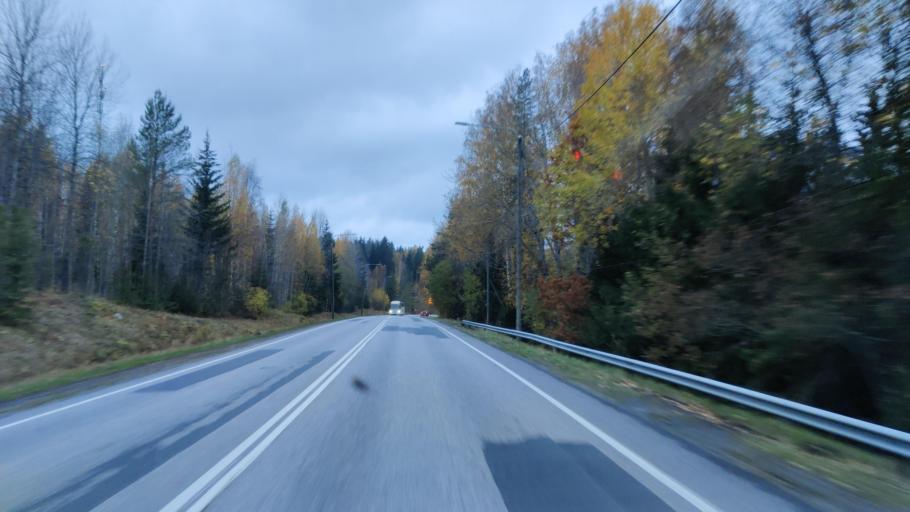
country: FI
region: Uusimaa
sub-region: Helsinki
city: Vihti
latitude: 60.3343
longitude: 24.2045
